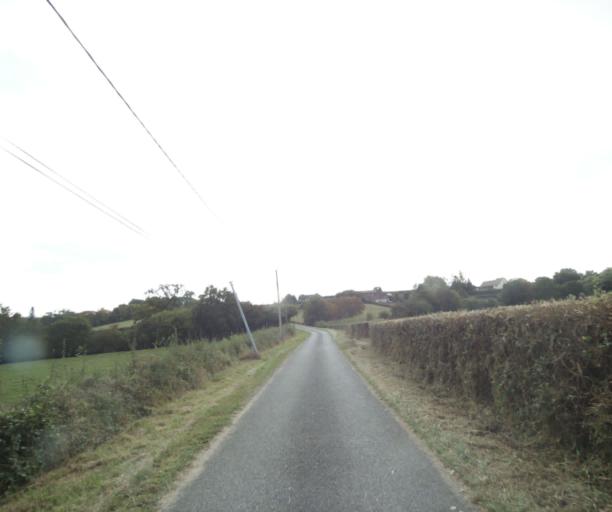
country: FR
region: Bourgogne
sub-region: Departement de Saone-et-Loire
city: Palinges
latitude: 46.4922
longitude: 4.2126
